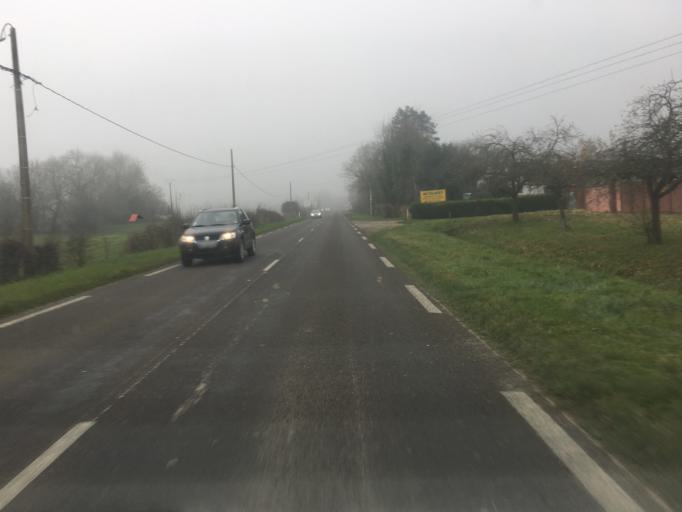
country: FR
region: Haute-Normandie
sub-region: Departement de la Seine-Maritime
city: Neufchatel-en-Bray
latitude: 49.7248
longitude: 1.4255
